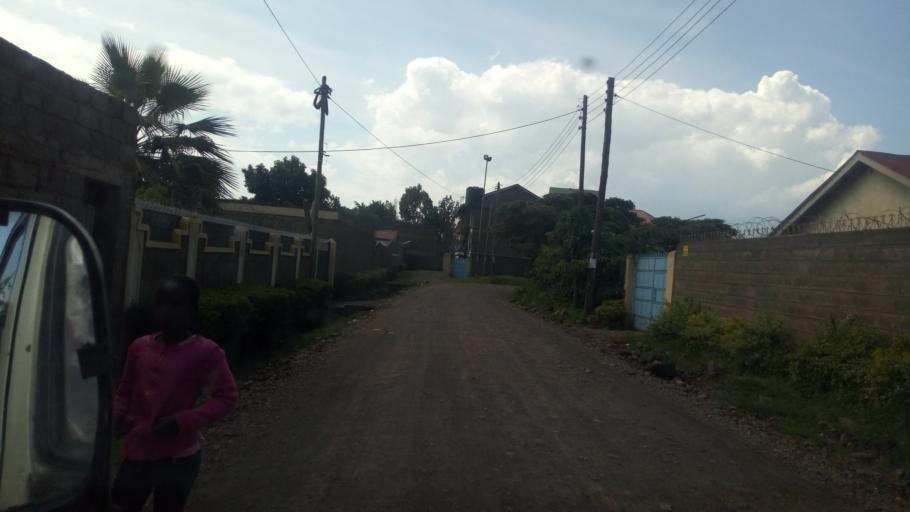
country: KE
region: Nakuru
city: Nakuru
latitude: -0.2776
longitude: 36.1042
